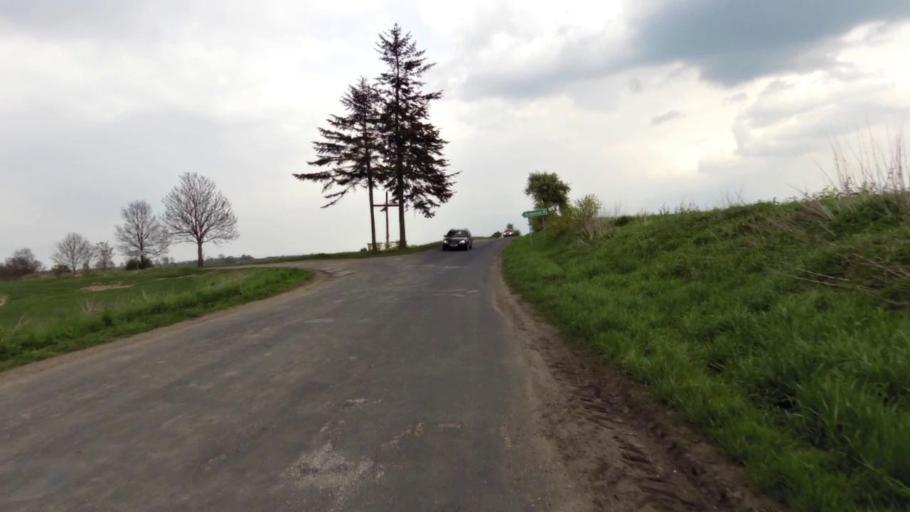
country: PL
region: West Pomeranian Voivodeship
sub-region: Powiat mysliborski
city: Mysliborz
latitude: 52.9232
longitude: 14.7677
